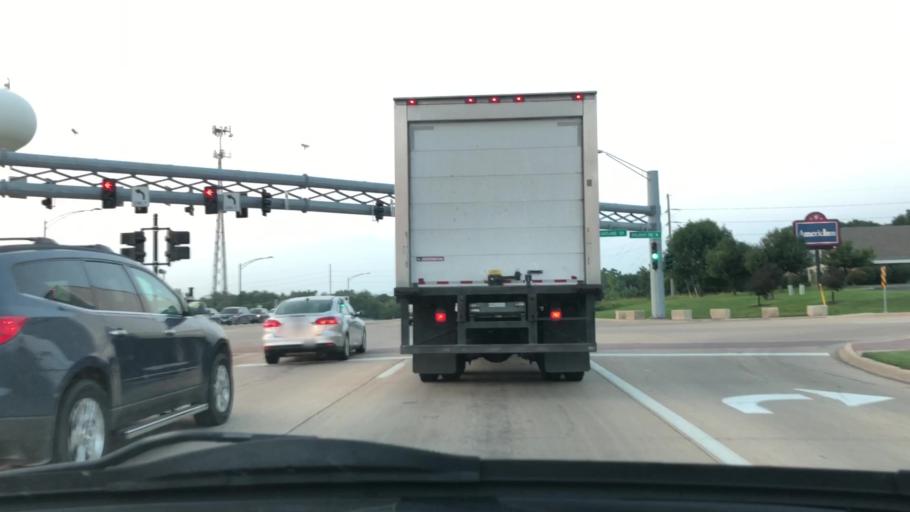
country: US
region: Iowa
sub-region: Johnson County
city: Coralville
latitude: 41.7002
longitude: -91.6082
